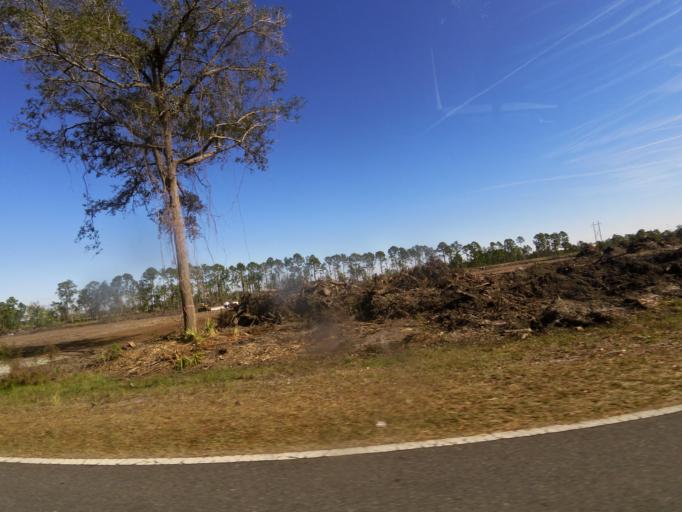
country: US
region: Georgia
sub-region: Glynn County
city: Brunswick
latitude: 31.1327
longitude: -81.5557
